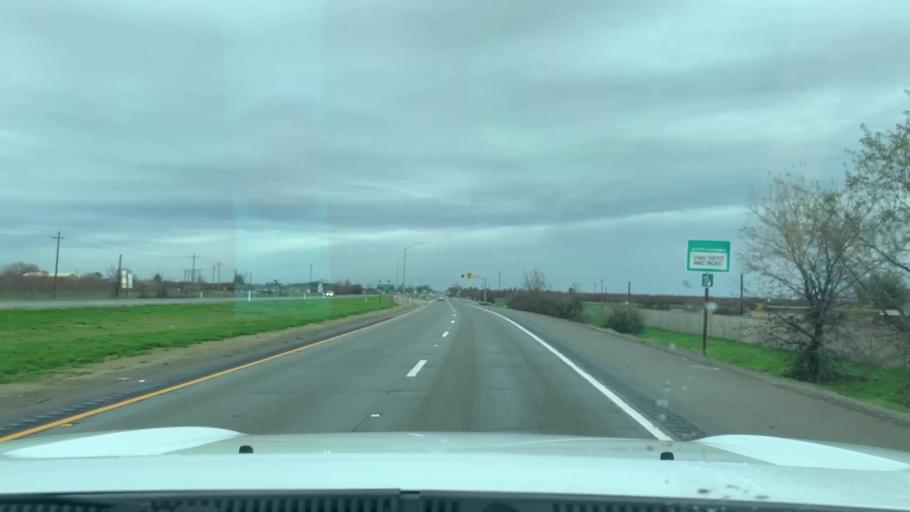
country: US
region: California
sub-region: Kings County
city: Lemoore
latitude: 36.3097
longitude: -119.8078
